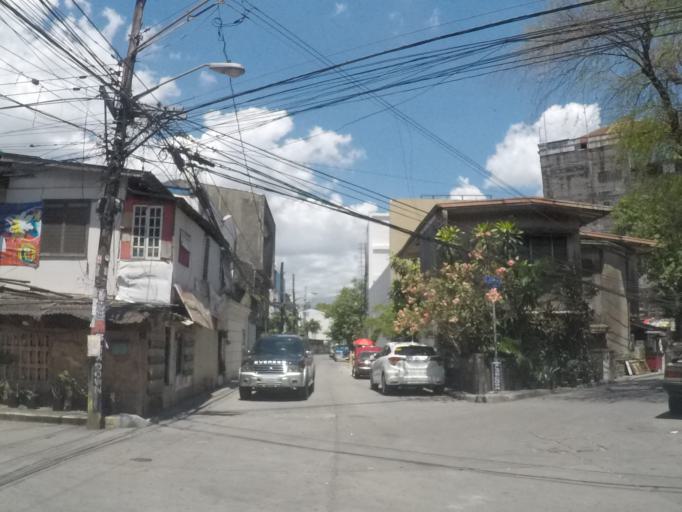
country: PH
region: Metro Manila
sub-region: San Juan
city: San Juan
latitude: 14.5978
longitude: 121.0266
